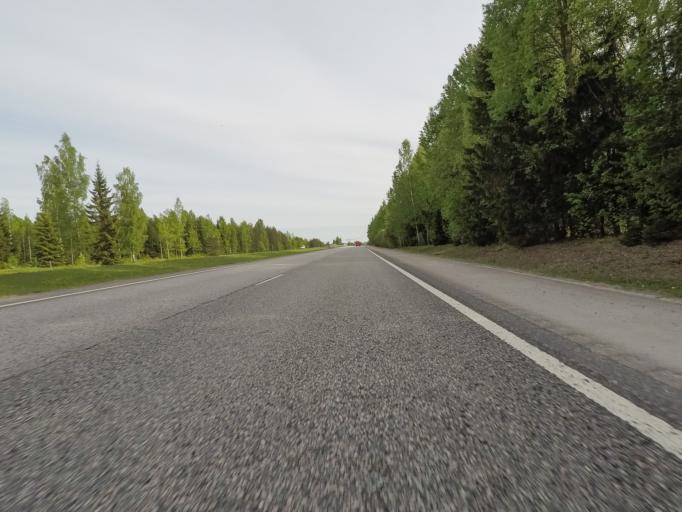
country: FI
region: Uusimaa
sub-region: Helsinki
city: Nurmijaervi
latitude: 60.5062
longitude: 24.8493
